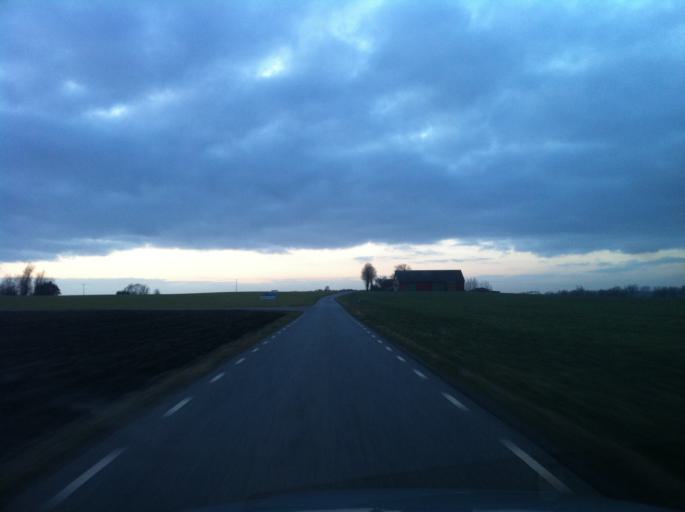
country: SE
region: Skane
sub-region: Svalovs Kommun
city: Teckomatorp
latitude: 55.8606
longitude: 13.0484
